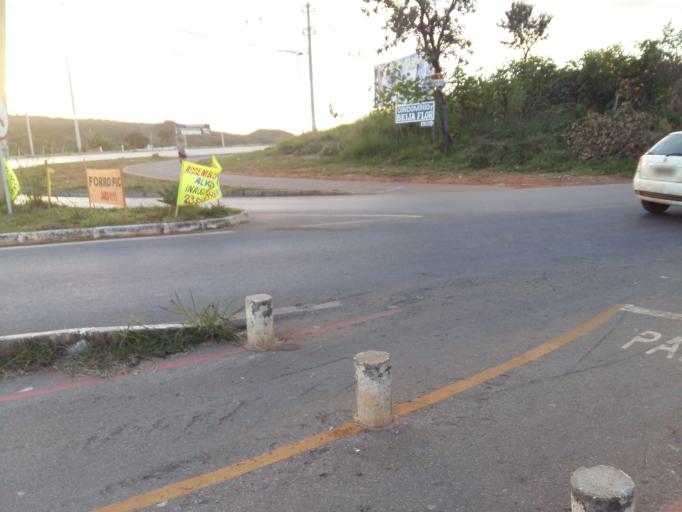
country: BR
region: Federal District
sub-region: Brasilia
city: Brasilia
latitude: -15.6561
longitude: -47.8458
